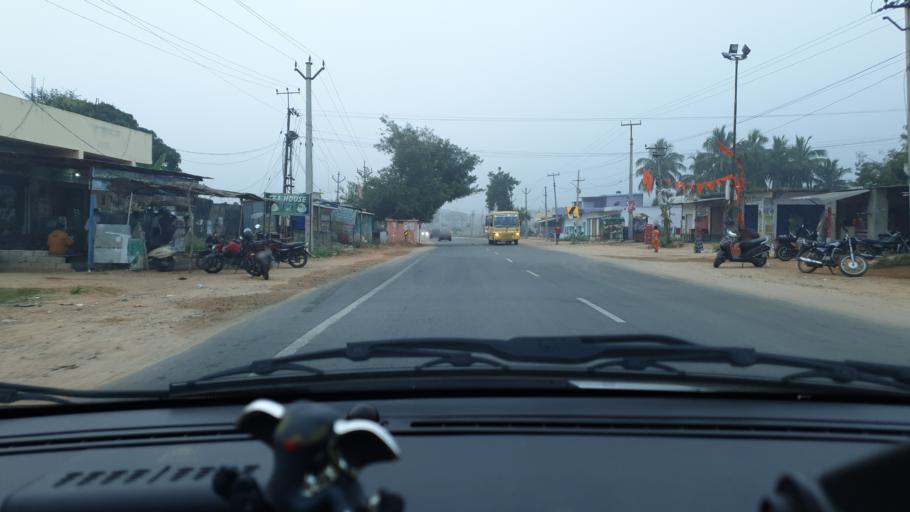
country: IN
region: Telangana
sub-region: Mahbubnagar
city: Farrukhnagar
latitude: 16.9262
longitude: 78.5274
